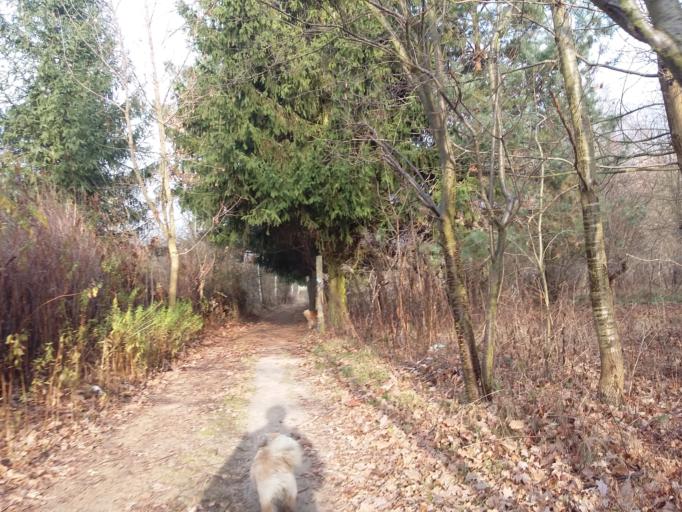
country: PL
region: Lodz Voivodeship
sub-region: Powiat pabianicki
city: Ksawerow
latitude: 51.7349
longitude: 19.4117
